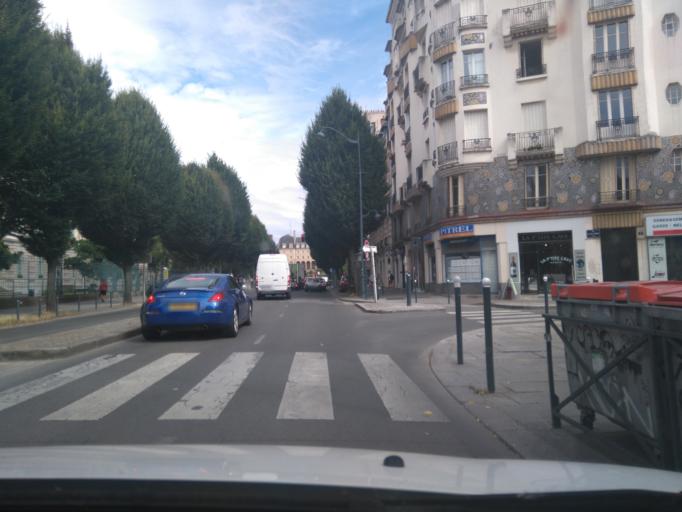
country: FR
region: Brittany
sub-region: Departement d'Ille-et-Vilaine
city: Rennes
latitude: 48.1086
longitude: -1.6737
